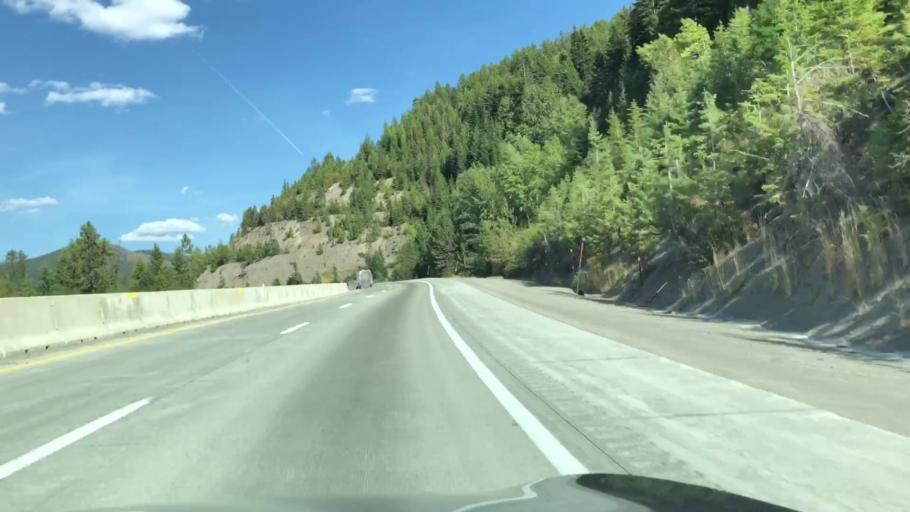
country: US
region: Idaho
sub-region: Shoshone County
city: Wallace
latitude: 47.4611
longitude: -115.7144
